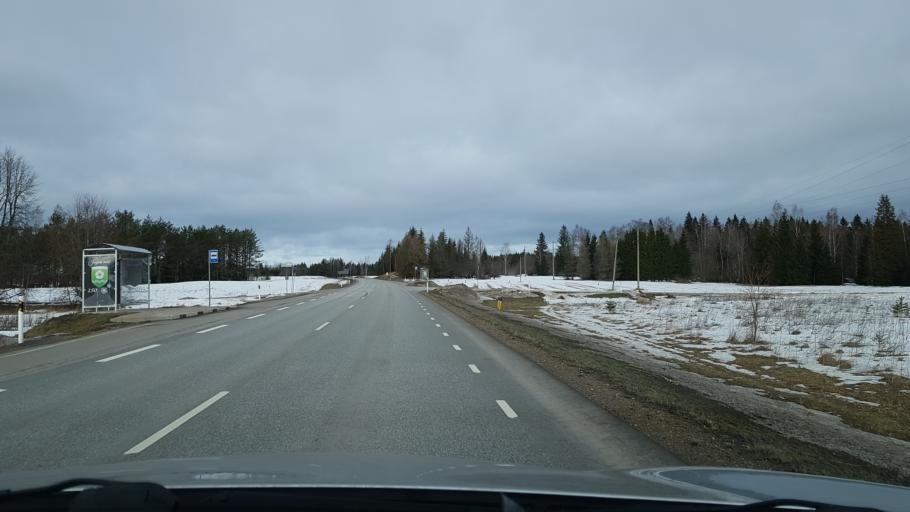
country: EE
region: Jogevamaa
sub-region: Jogeva linn
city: Jogeva
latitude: 58.7736
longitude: 26.3262
